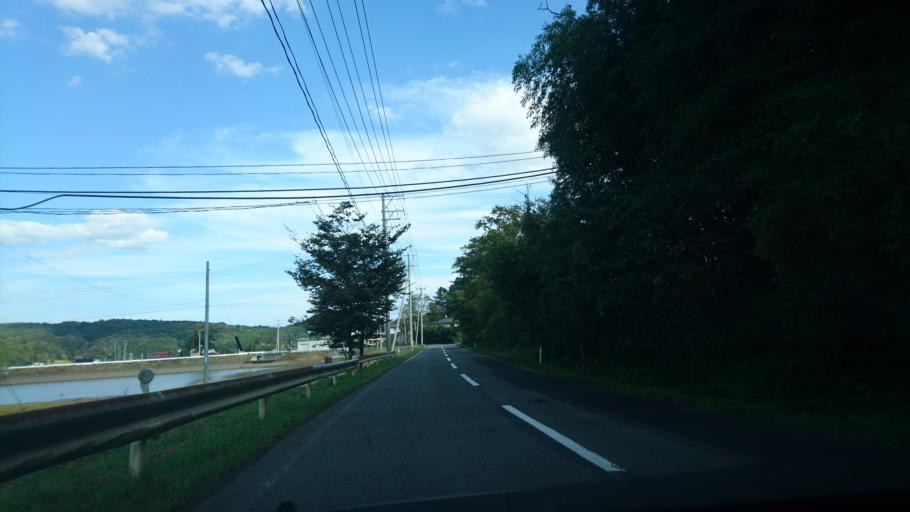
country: JP
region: Iwate
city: Ichinoseki
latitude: 38.8351
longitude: 141.2319
